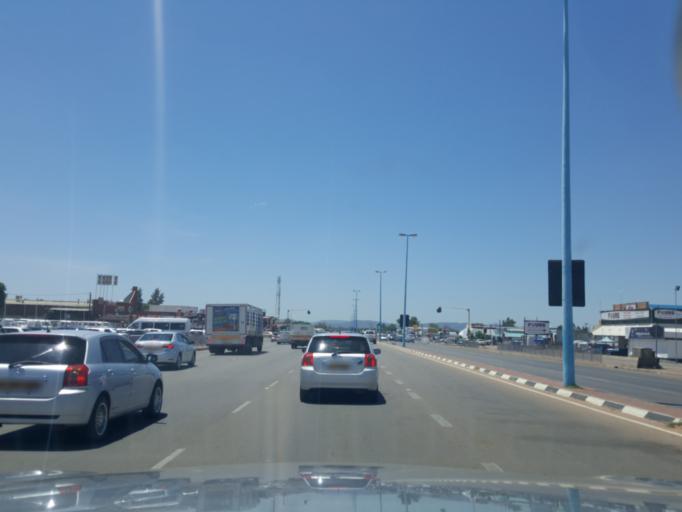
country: BW
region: Kweneng
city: Mogoditshane
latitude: -24.6207
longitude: 25.8666
